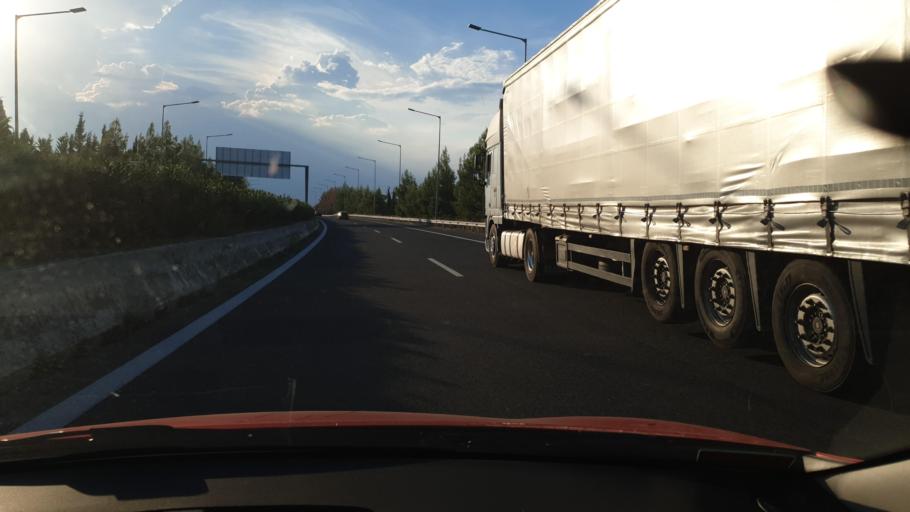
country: GR
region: Thessaly
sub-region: Nomos Magnisias
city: Velestino
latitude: 39.3983
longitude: 22.7599
